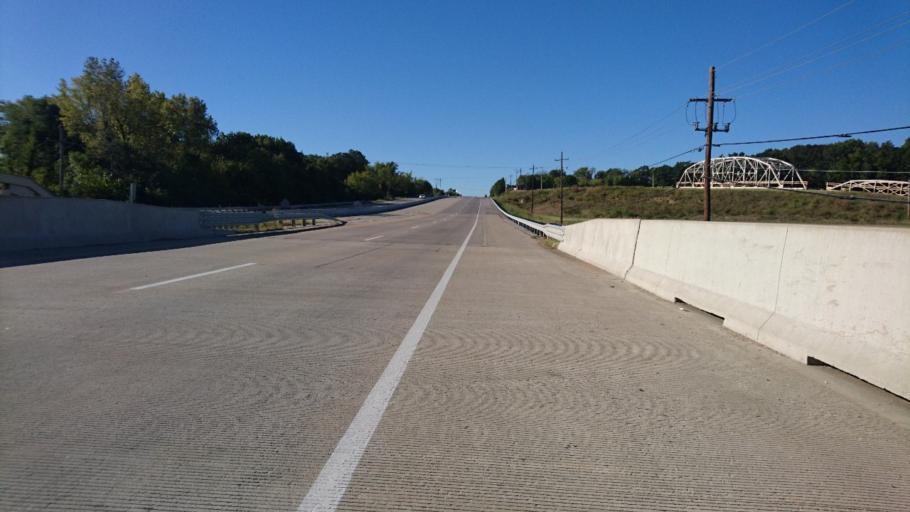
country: US
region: Oklahoma
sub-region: Rogers County
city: Catoosa
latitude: 36.2085
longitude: -95.7251
